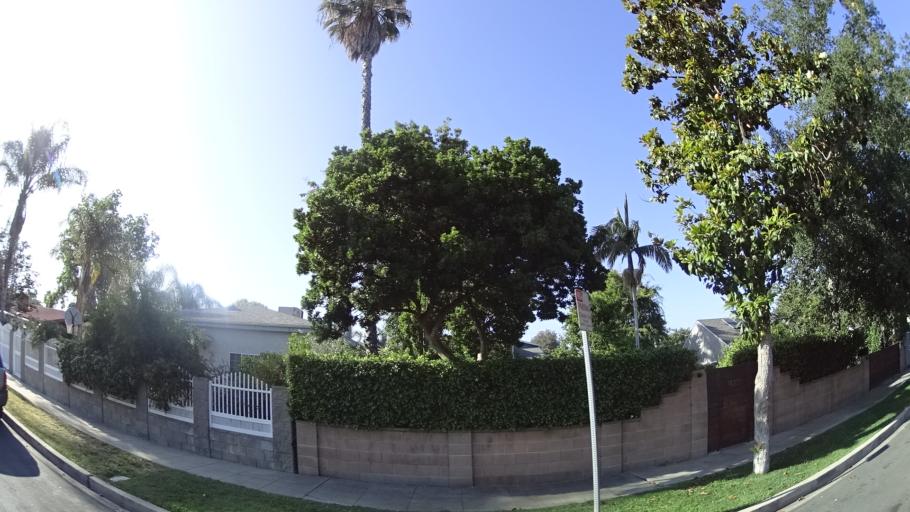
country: US
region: California
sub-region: Los Angeles County
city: Van Nuys
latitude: 34.1767
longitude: -118.4435
